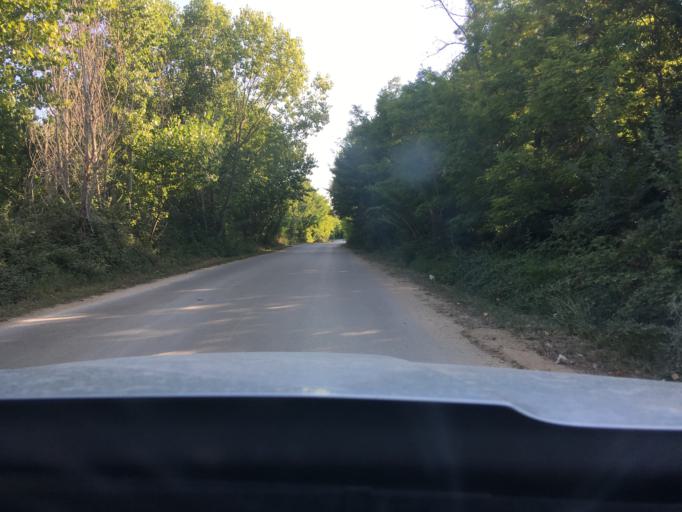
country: HR
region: Zadarska
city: Privlaka
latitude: 44.2504
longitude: 15.1515
